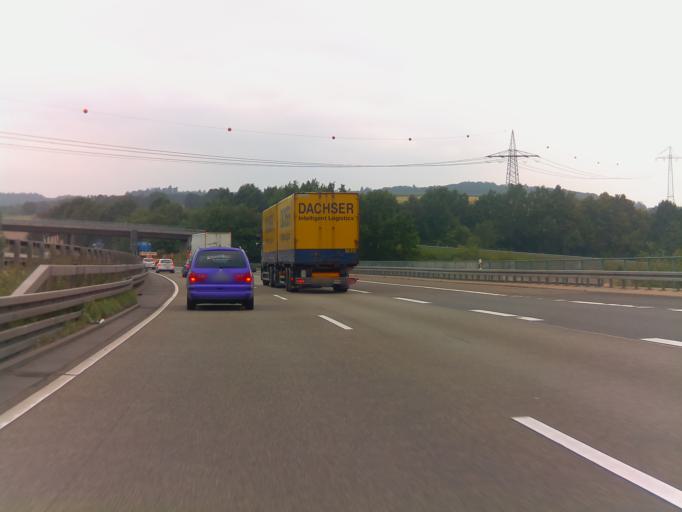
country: DE
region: Hesse
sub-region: Regierungsbezirk Kassel
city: Niederaula
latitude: 50.7753
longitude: 9.5862
